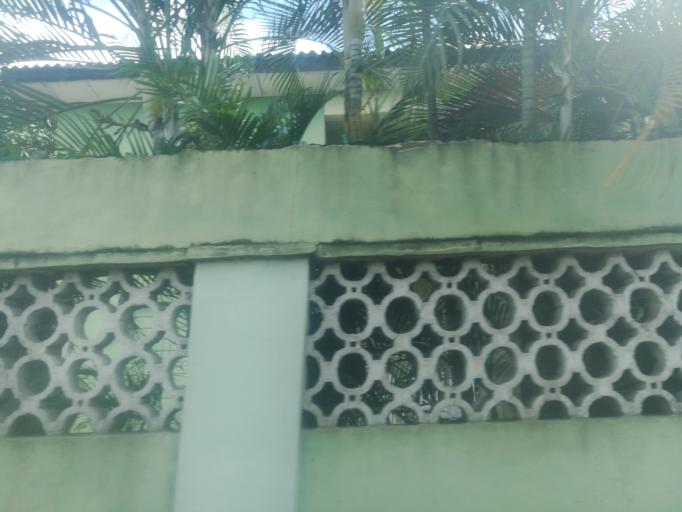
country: NG
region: Lagos
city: Somolu
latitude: 6.5493
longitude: 3.3679
